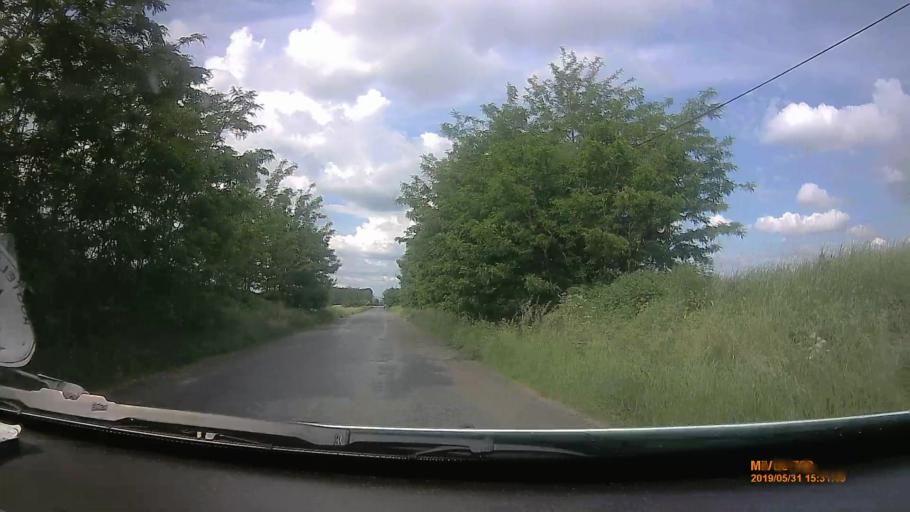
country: HU
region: Borsod-Abauj-Zemplen
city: Prugy
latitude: 48.0659
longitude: 21.2344
